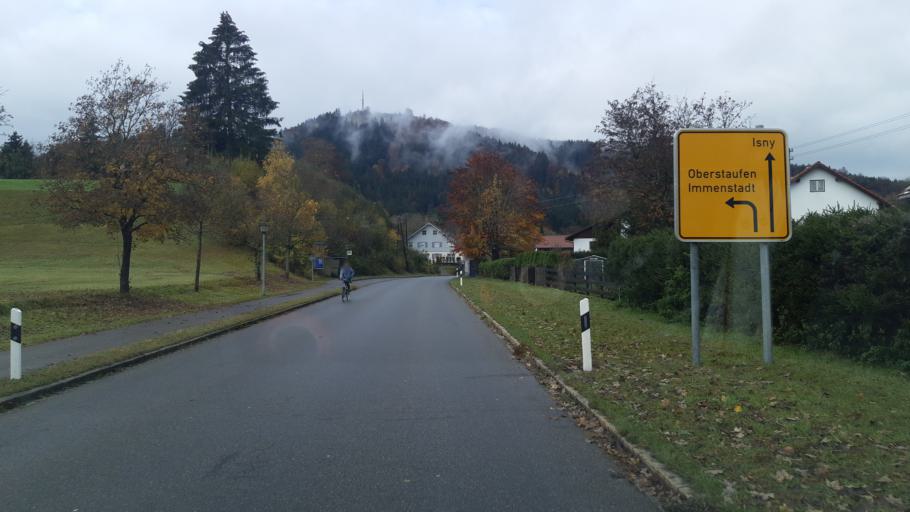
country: DE
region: Bavaria
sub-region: Swabia
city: Weitnau
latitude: 47.6409
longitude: 10.0962
